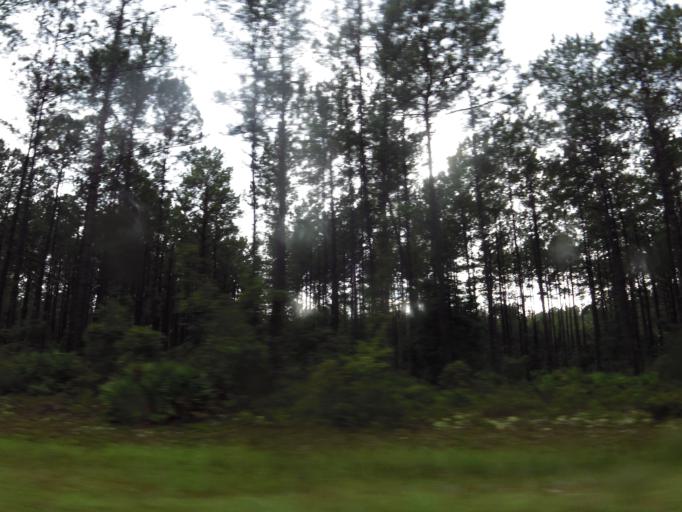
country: US
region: Georgia
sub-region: Wayne County
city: Jesup
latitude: 31.5487
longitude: -81.8710
